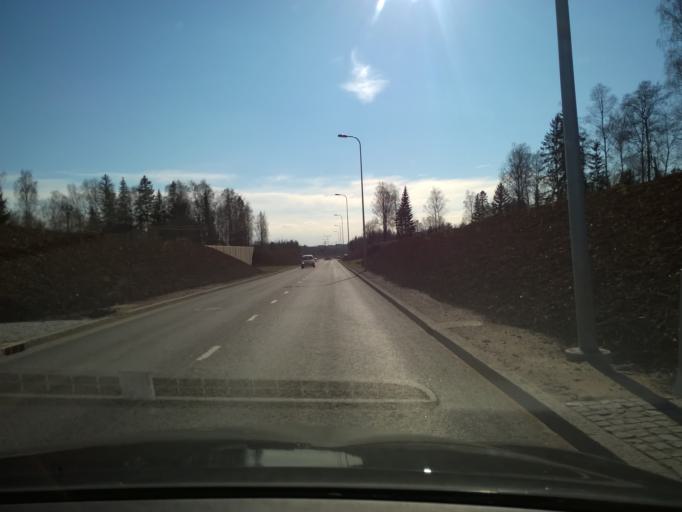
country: FI
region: Uusimaa
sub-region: Helsinki
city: Kilo
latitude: 60.1908
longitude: 24.7853
